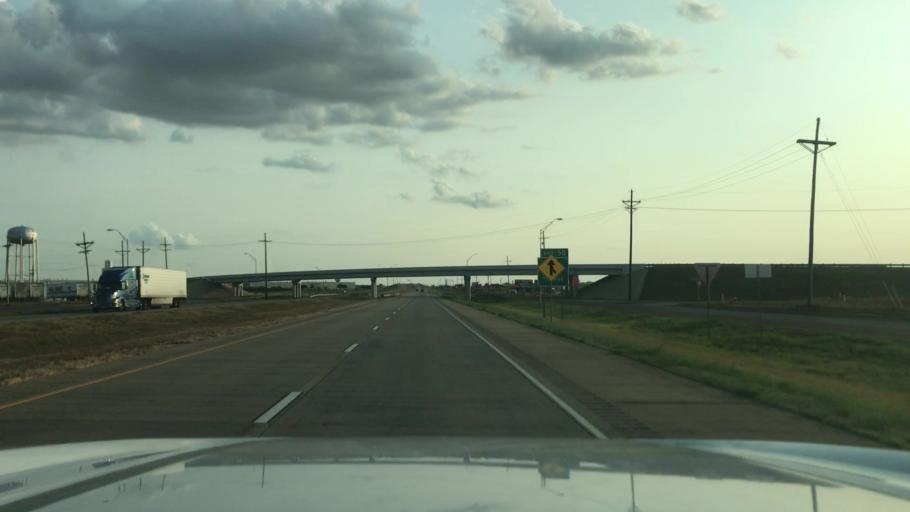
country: US
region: Texas
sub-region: Hale County
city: Seth Ward
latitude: 34.2207
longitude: -101.7239
